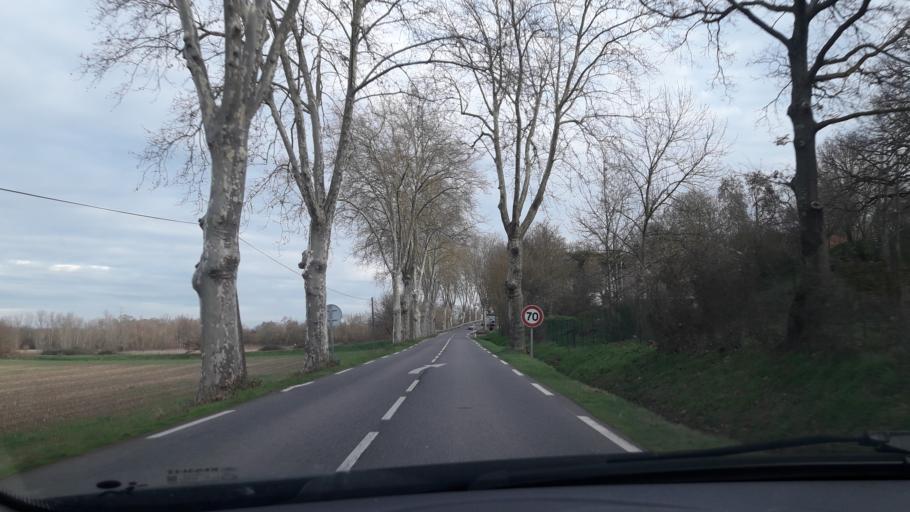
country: FR
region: Midi-Pyrenees
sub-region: Departement de la Haute-Garonne
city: Grenade
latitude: 43.7440
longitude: 1.2650
